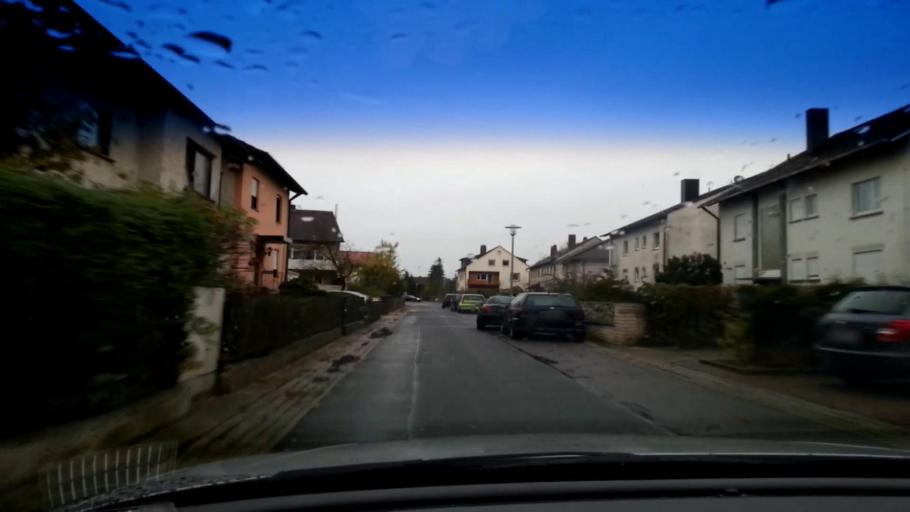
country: DE
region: Bavaria
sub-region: Upper Franconia
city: Hallstadt
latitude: 49.9239
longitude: 10.8843
